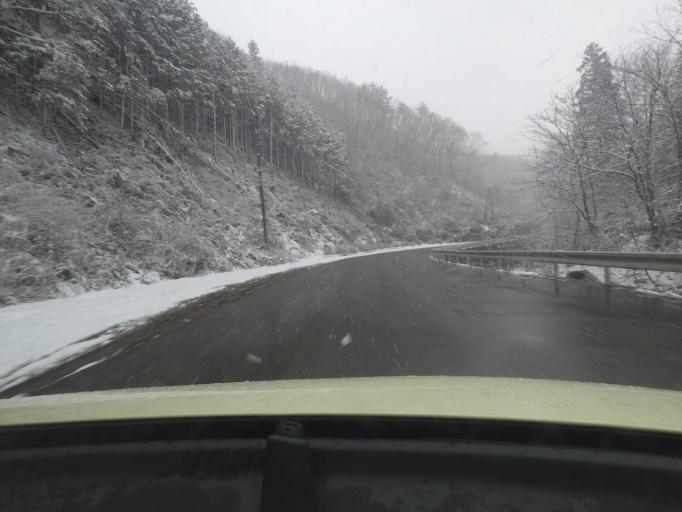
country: JP
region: Gifu
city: Takayama
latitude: 36.1370
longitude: 137.3351
